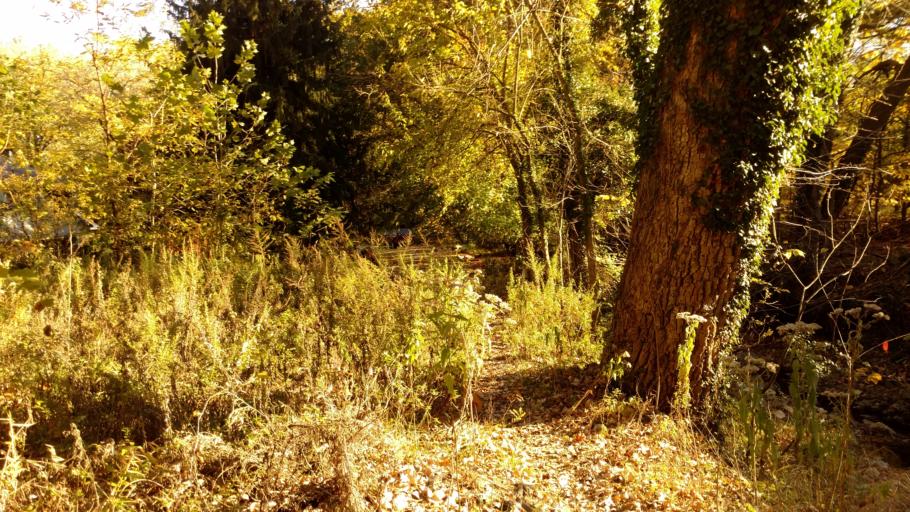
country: US
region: Maryland
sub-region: Baltimore County
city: Charlestown
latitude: 39.2643
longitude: -76.7147
